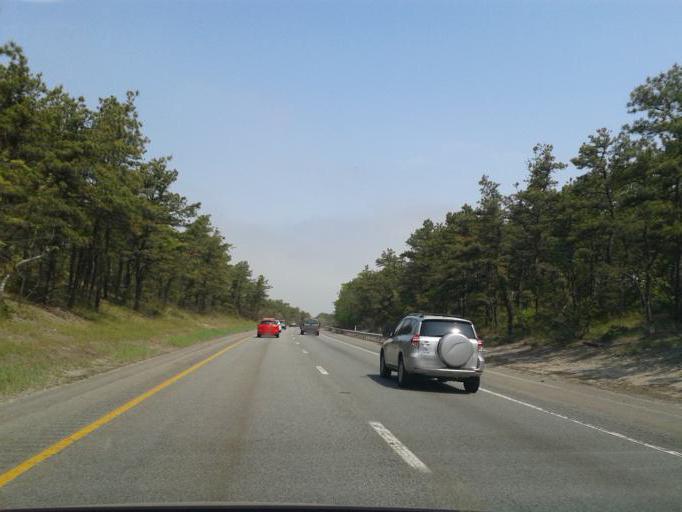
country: US
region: Massachusetts
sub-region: Plymouth County
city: White Island Shores
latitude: 41.8810
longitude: -70.6085
